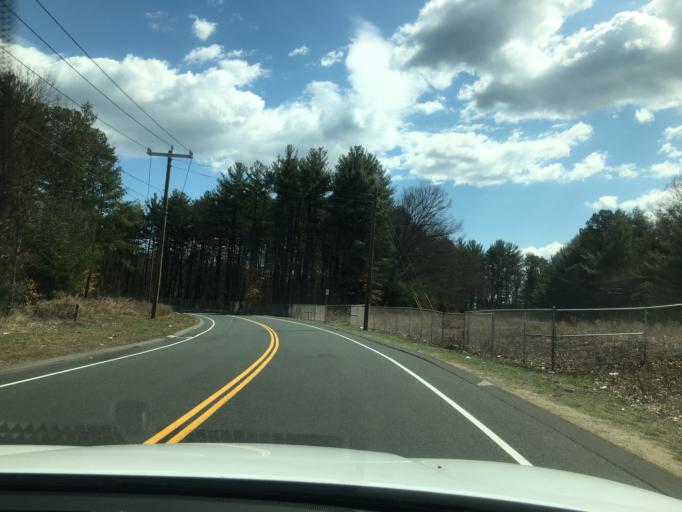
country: US
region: Connecticut
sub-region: Hartford County
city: Blue Hills
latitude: 41.8645
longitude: -72.7114
